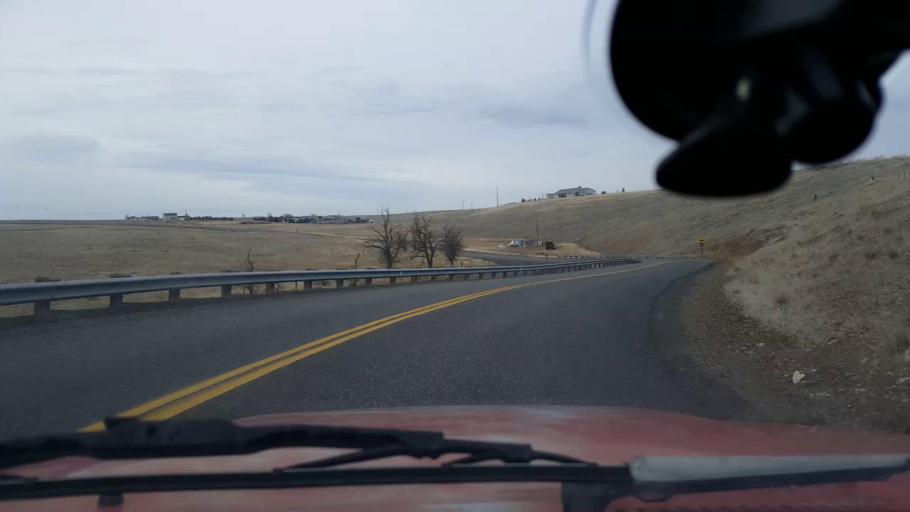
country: US
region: Washington
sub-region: Asotin County
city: Clarkston Heights-Vineland
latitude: 46.3776
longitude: -117.1470
